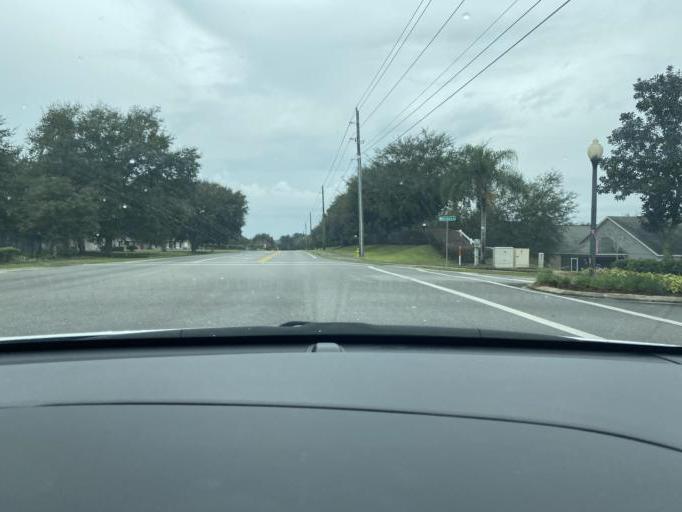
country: US
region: Florida
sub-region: Lake County
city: Groveland
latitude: 28.5769
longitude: -81.8635
